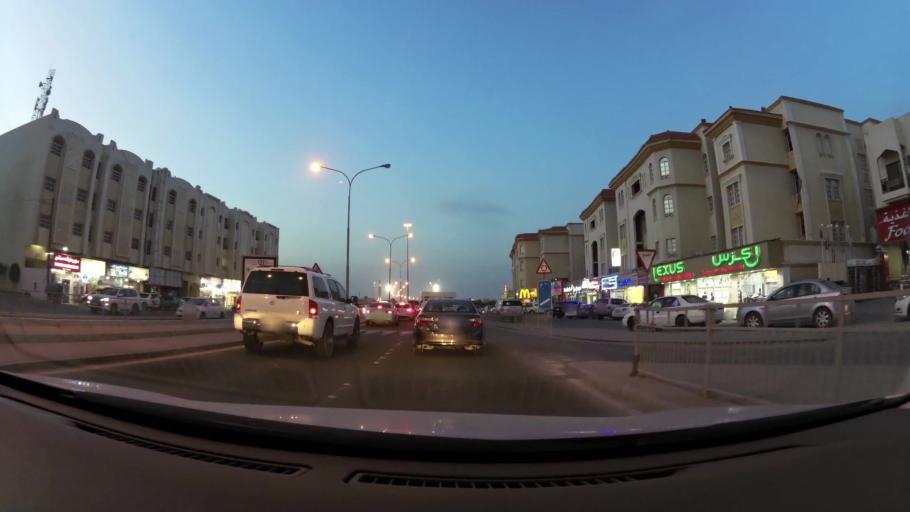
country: QA
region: Al Wakrah
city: Al Wakrah
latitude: 25.1710
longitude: 51.5978
